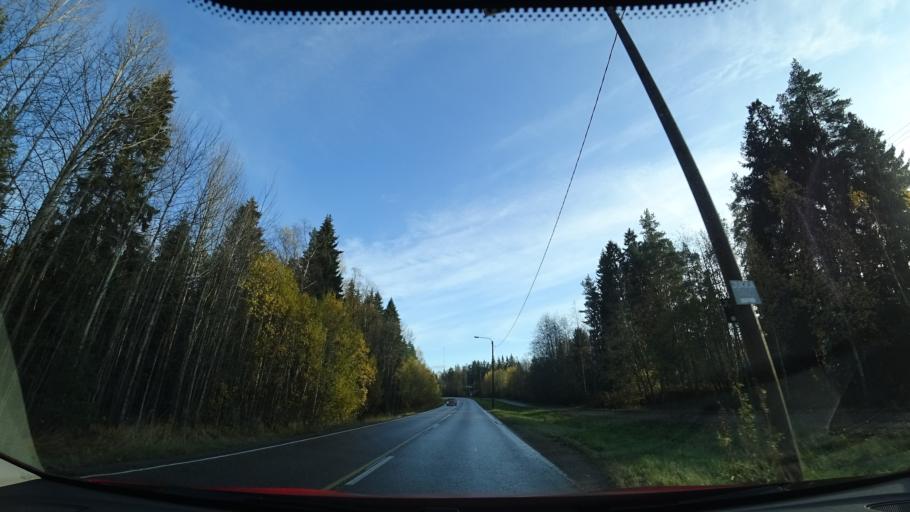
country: FI
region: Uusimaa
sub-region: Helsinki
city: Sibbo
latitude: 60.2709
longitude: 25.2028
